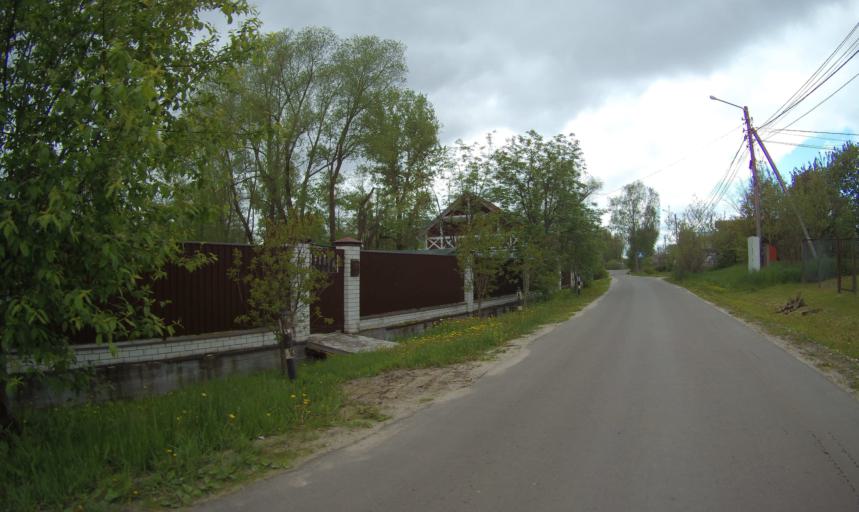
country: RU
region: Moskovskaya
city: Rechitsy
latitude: 55.5401
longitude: 38.4239
